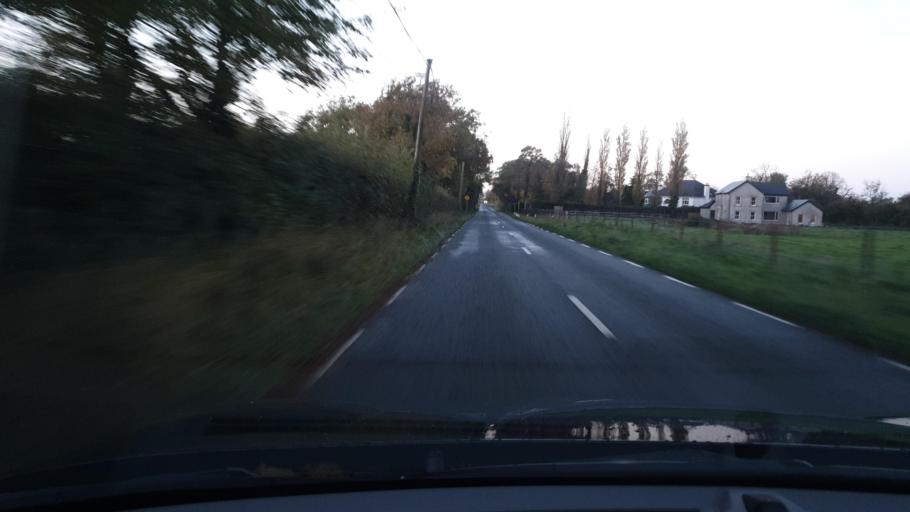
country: IE
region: Leinster
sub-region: An Mhi
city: Ratoath
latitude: 53.4894
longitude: -6.4354
